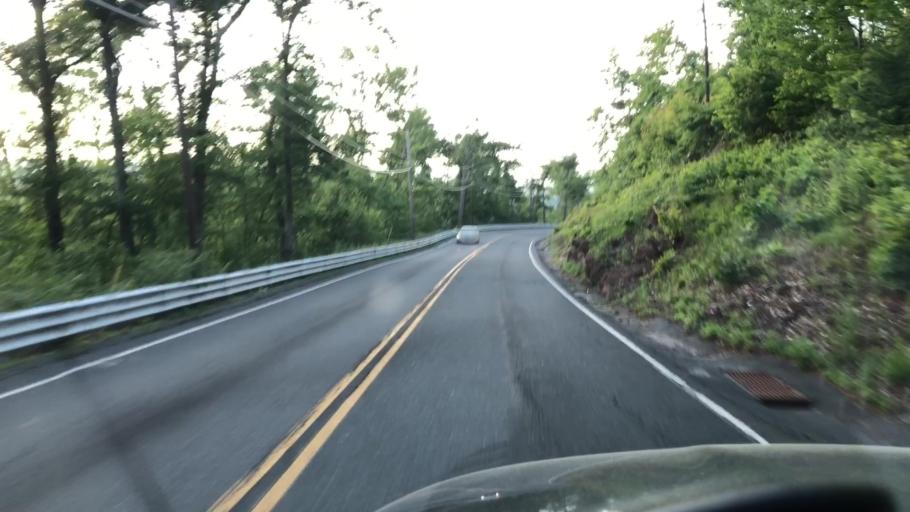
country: US
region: Massachusetts
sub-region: Hampshire County
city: Easthampton
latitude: 42.2389
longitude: -72.6523
